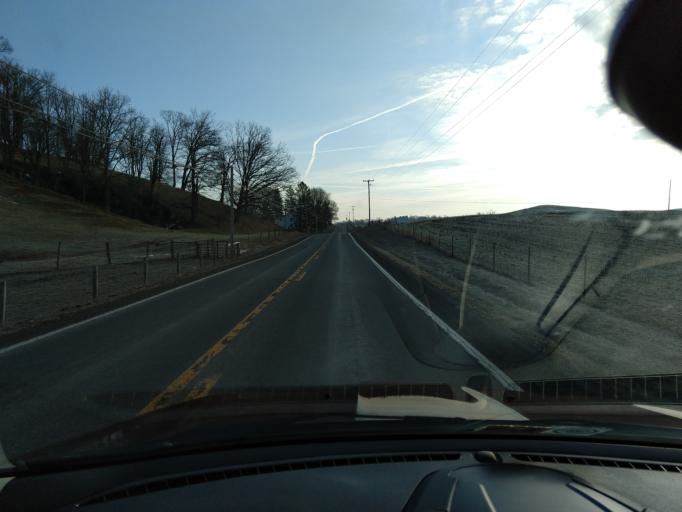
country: US
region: West Virginia
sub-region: Pocahontas County
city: Marlinton
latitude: 38.1272
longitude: -80.2303
